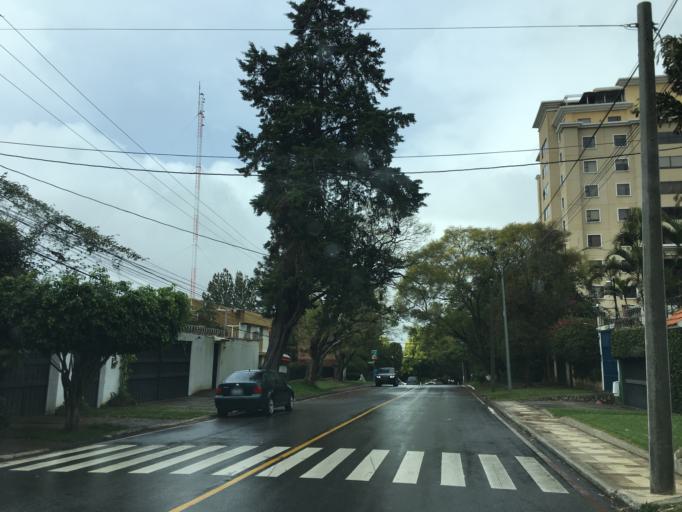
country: GT
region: Guatemala
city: Santa Catarina Pinula
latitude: 14.5928
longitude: -90.4954
